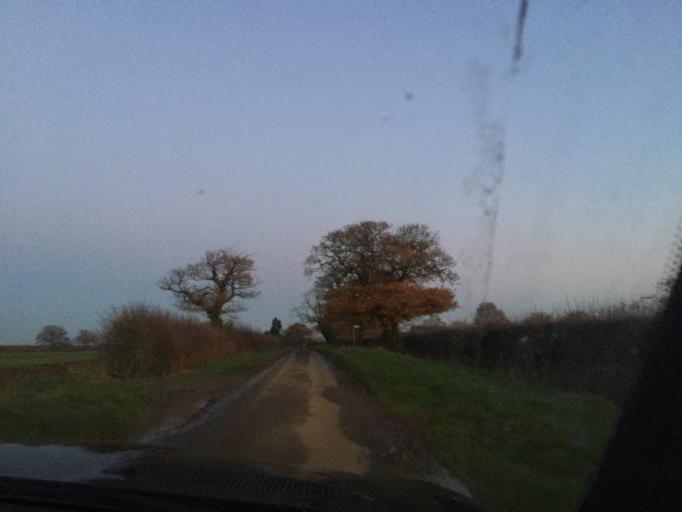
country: GB
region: England
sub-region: Northamptonshire
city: Silverstone
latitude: 52.0890
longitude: -1.0988
